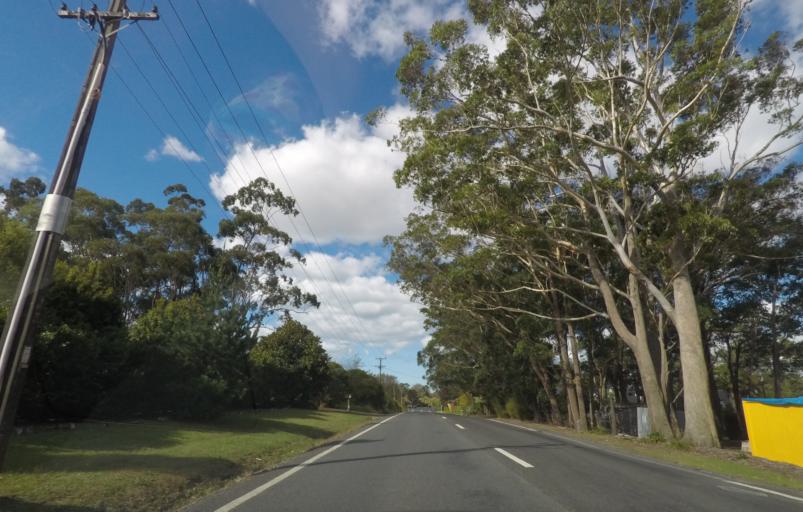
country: NZ
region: Auckland
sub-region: Auckland
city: Rothesay Bay
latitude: -36.5985
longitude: 174.6545
